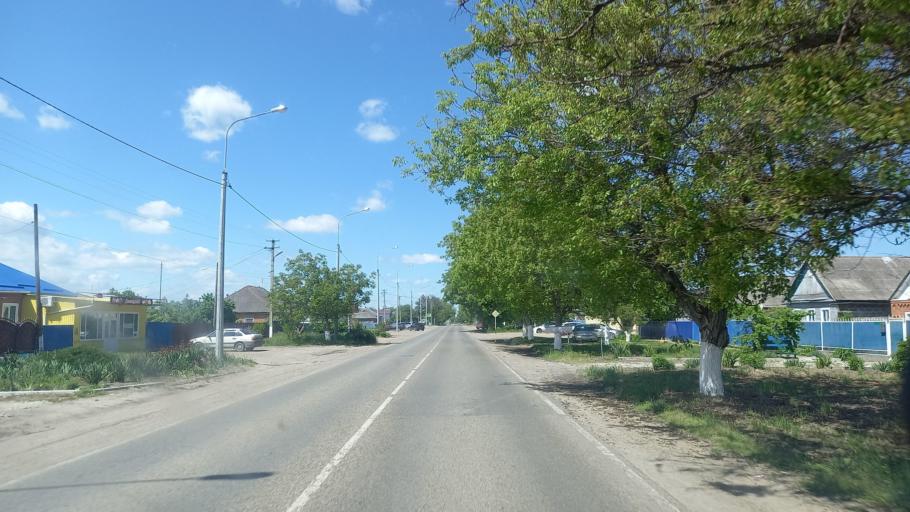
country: RU
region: Krasnodarskiy
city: Novoukrainskoye
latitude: 45.3804
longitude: 40.5129
